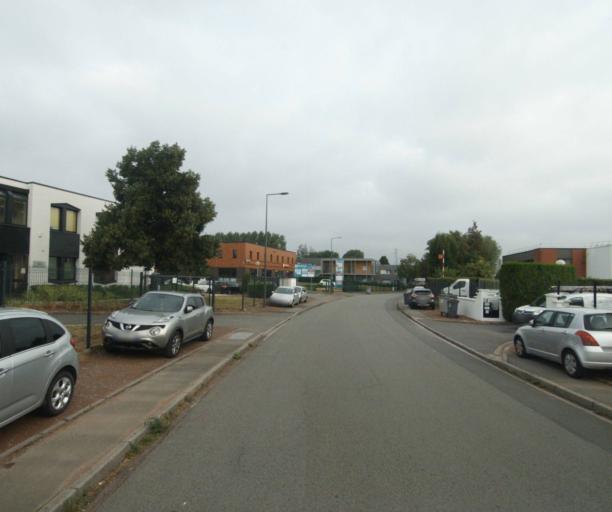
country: FR
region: Nord-Pas-de-Calais
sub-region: Departement du Nord
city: Mons-en-Baroeul
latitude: 50.6504
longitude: 3.1224
